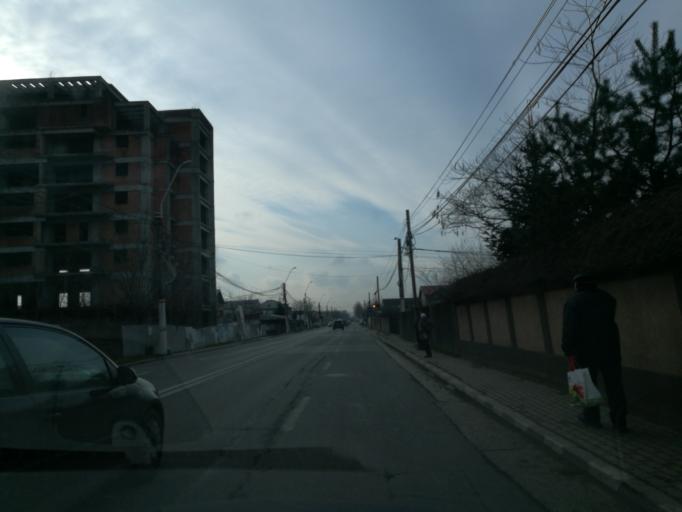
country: RO
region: Ilfov
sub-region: Voluntari City
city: Voluntari
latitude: 44.4970
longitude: 26.1764
